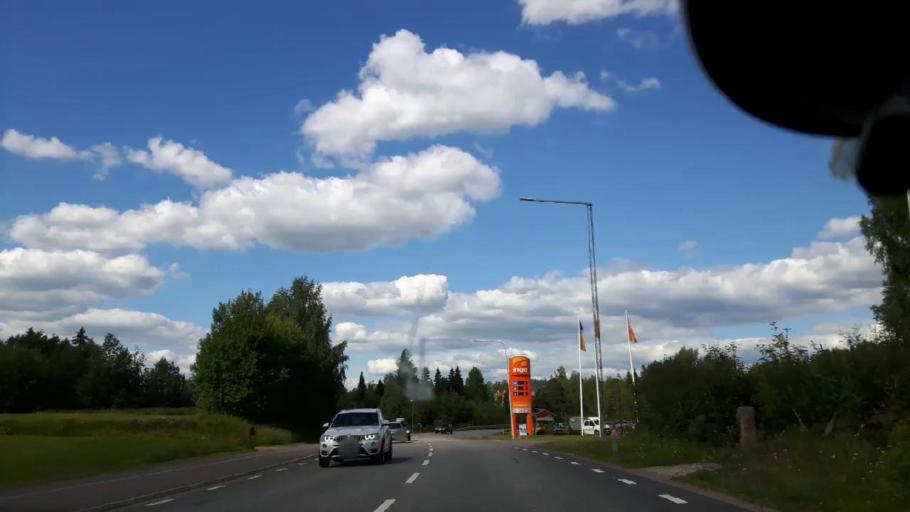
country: SE
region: Jaemtland
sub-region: Ragunda Kommun
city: Hammarstrand
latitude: 63.0092
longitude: 16.6629
